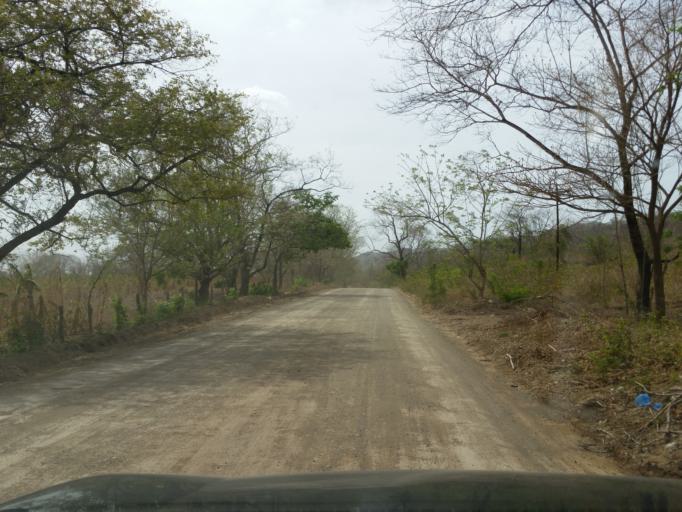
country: NI
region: Rivas
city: Tola
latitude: 11.4432
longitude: -86.0437
